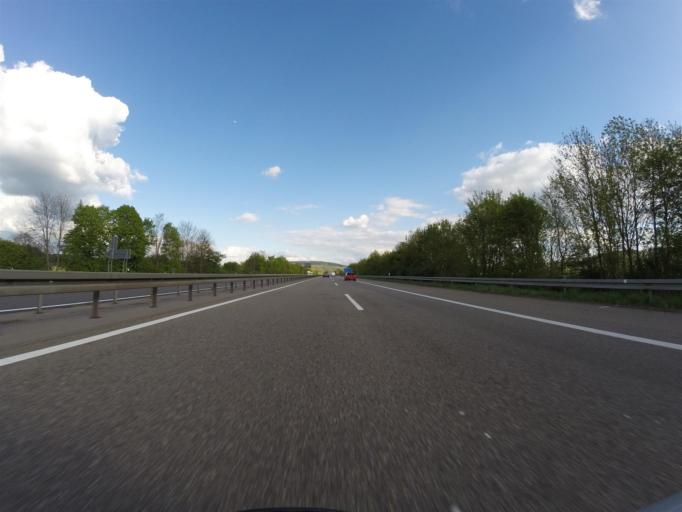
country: DE
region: Saarland
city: Merzig
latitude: 49.4570
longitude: 6.6075
